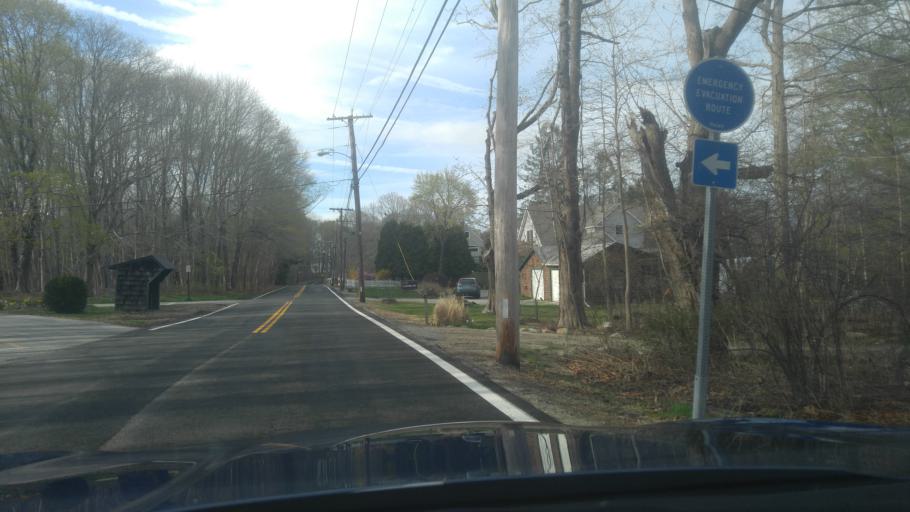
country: US
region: Rhode Island
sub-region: Newport County
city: Jamestown
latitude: 41.5647
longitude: -71.3648
